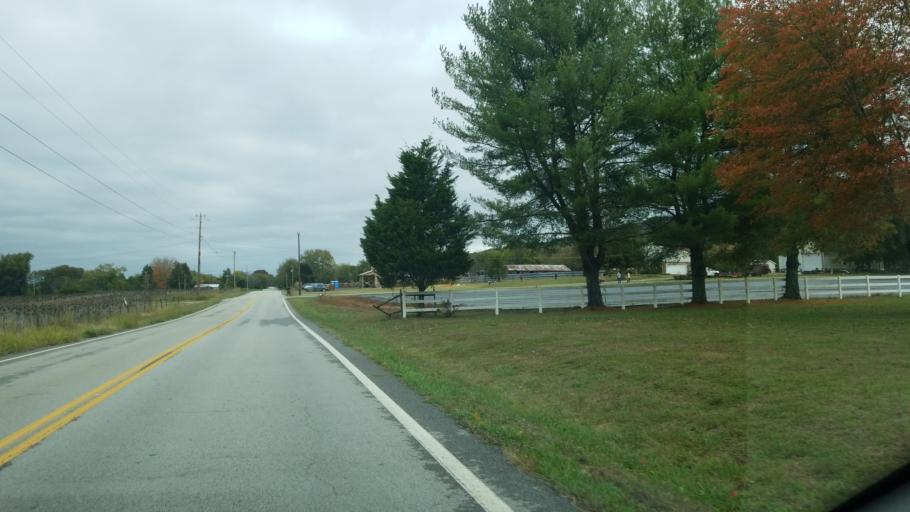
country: US
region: Tennessee
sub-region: Hamilton County
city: Lakesite
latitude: 35.1957
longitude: -85.0164
